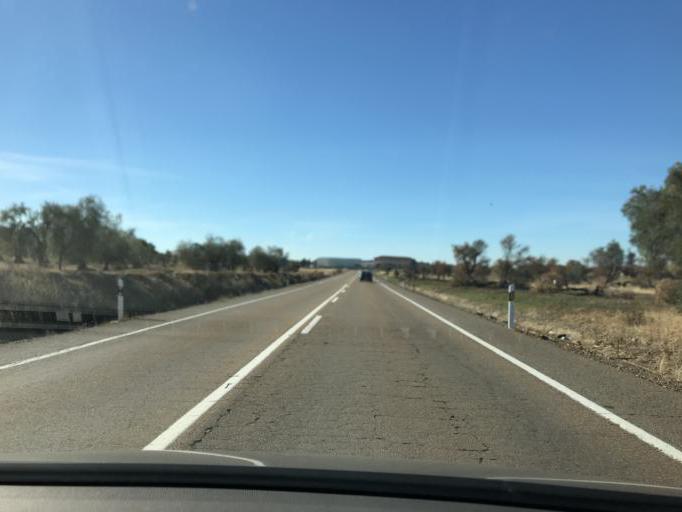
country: ES
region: Extremadura
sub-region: Provincia de Badajoz
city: Azuaga
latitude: 38.2656
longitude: -5.6926
